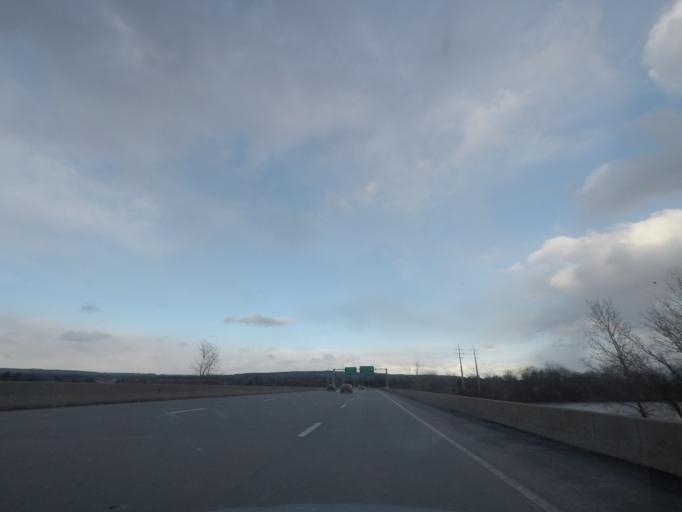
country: US
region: New York
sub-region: Oneida County
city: Utica
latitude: 43.1191
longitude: -75.2313
